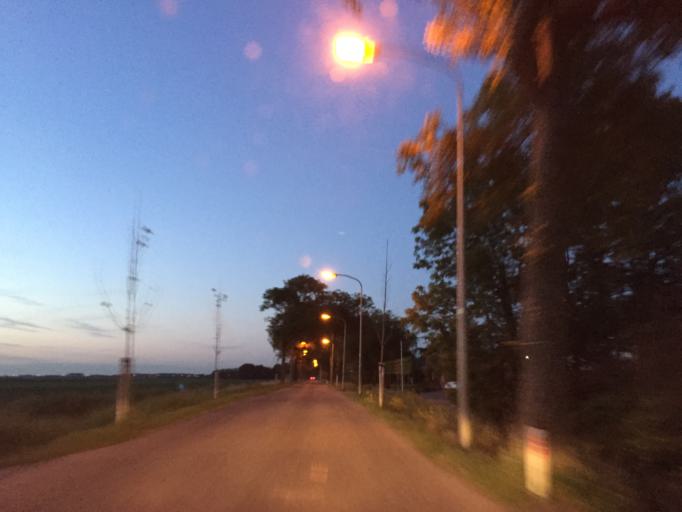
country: NL
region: South Holland
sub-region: Gemeente Waddinxveen
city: Groenswaard
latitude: 52.0297
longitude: 4.6165
